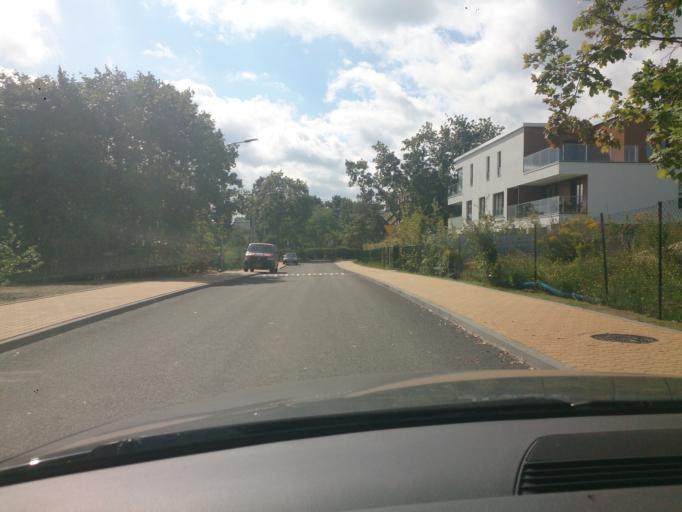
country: PL
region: Pomeranian Voivodeship
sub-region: Sopot
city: Sopot
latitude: 54.4807
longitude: 18.5559
